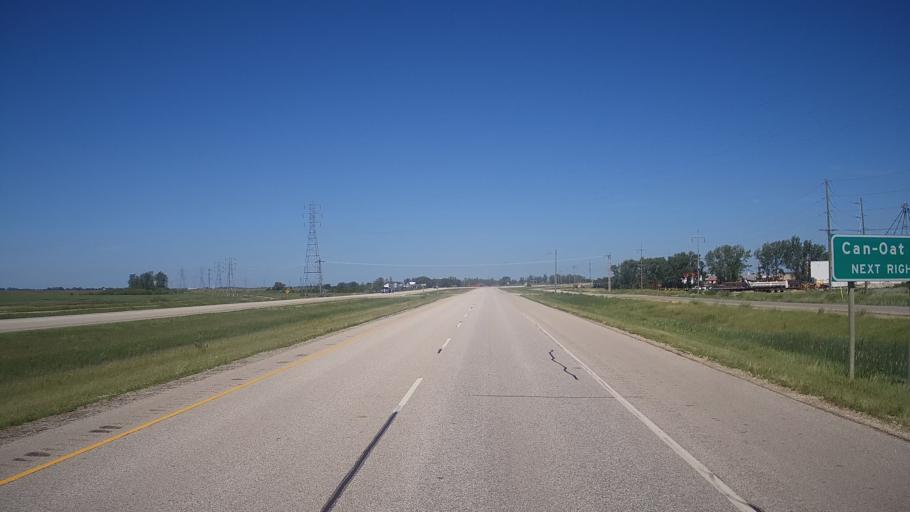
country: CA
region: Manitoba
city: Portage la Prairie
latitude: 49.9597
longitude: -98.3435
